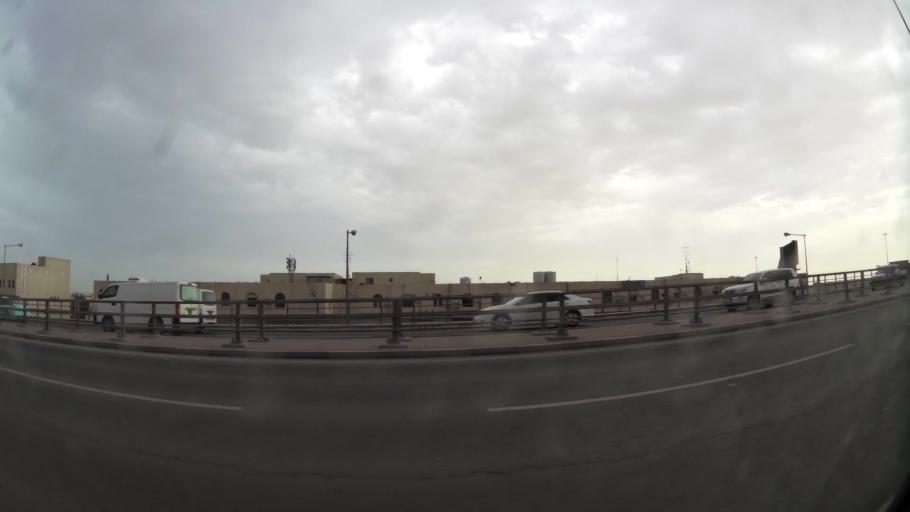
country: QA
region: Baladiyat ad Dawhah
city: Doha
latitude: 25.2647
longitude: 51.4981
